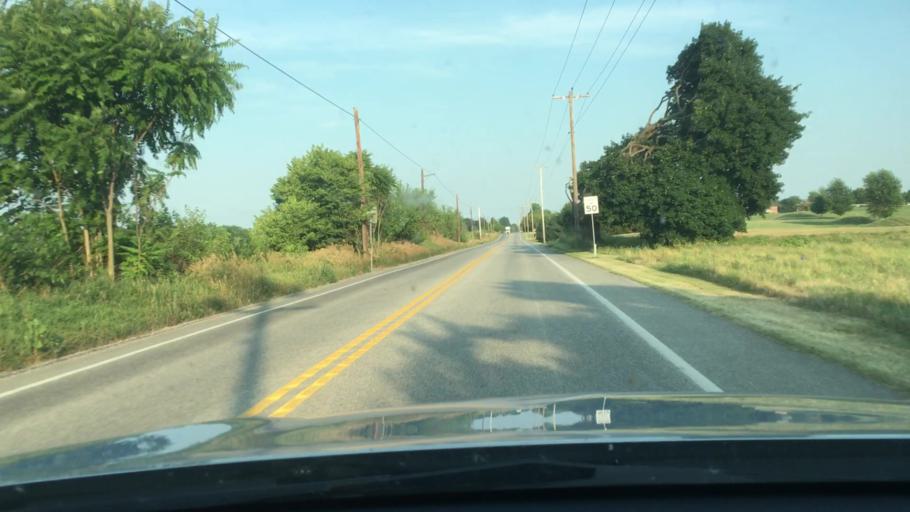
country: US
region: Pennsylvania
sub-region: Cumberland County
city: Boiling Springs
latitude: 40.1859
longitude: -77.1485
